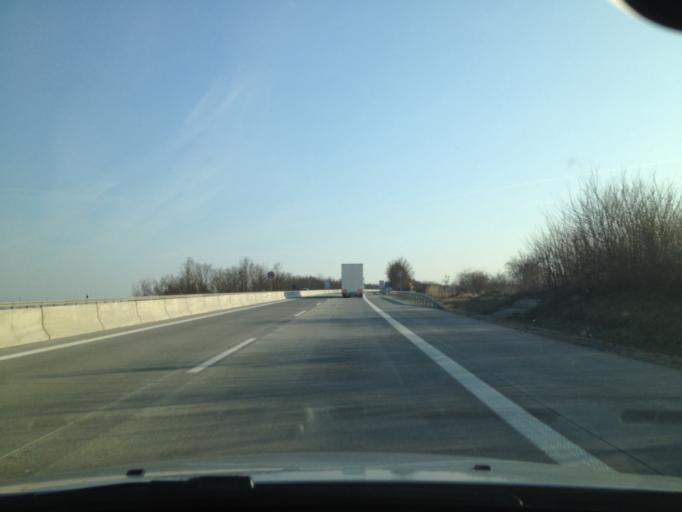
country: DE
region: Bavaria
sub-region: Regierungsbezirk Unterfranken
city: Martinsheim
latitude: 49.6006
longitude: 10.1744
